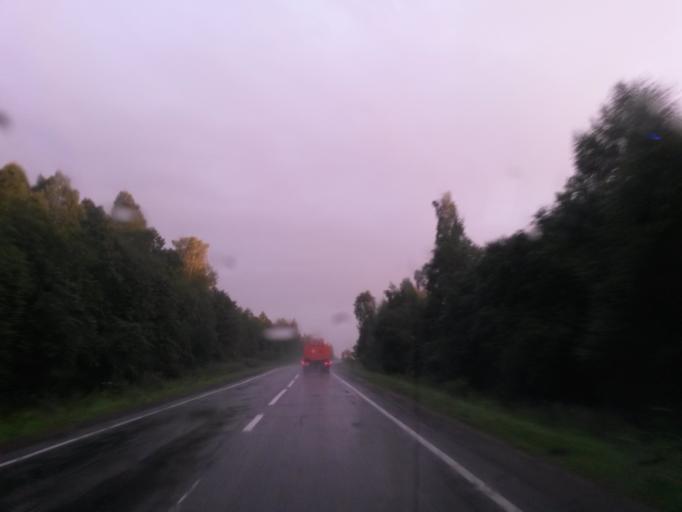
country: RU
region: Jaroslavl
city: Gavrilov-Yam
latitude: 57.3825
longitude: 39.9107
